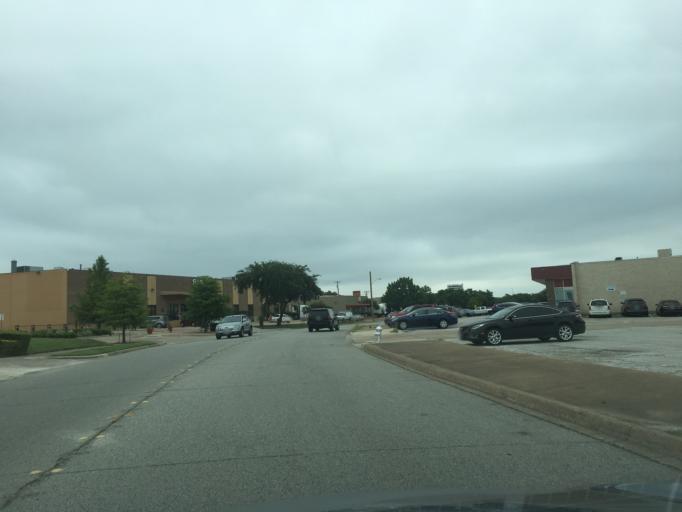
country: US
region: Texas
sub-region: Dallas County
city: Richardson
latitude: 32.9413
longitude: -96.7398
